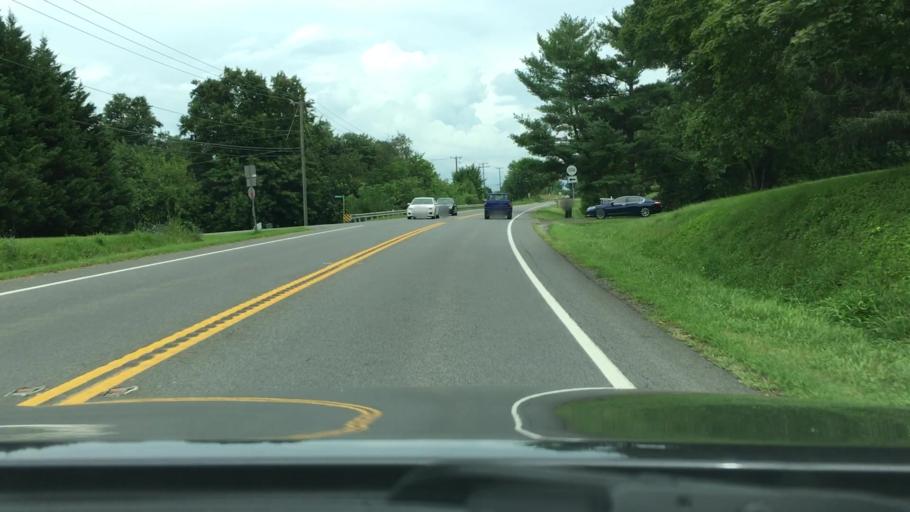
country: US
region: Virginia
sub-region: Orange County
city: Orange
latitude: 38.2452
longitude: -78.0808
